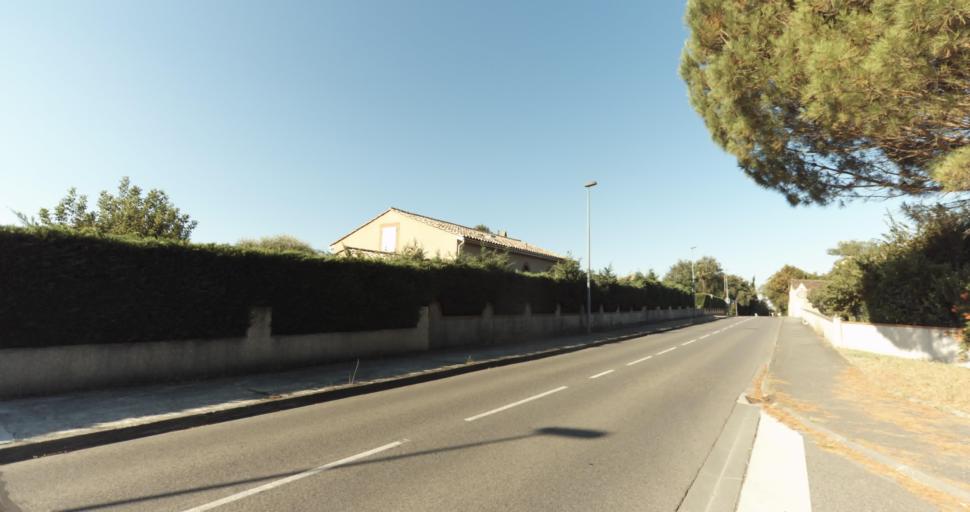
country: FR
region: Midi-Pyrenees
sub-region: Departement de la Haute-Garonne
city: L'Union
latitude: 43.6636
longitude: 1.4892
